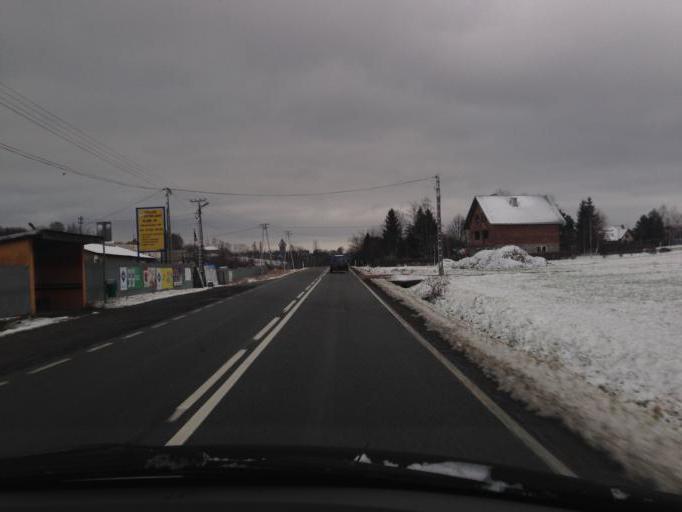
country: PL
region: Lesser Poland Voivodeship
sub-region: Powiat tarnowski
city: Siemiechow
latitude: 49.8503
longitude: 20.9239
